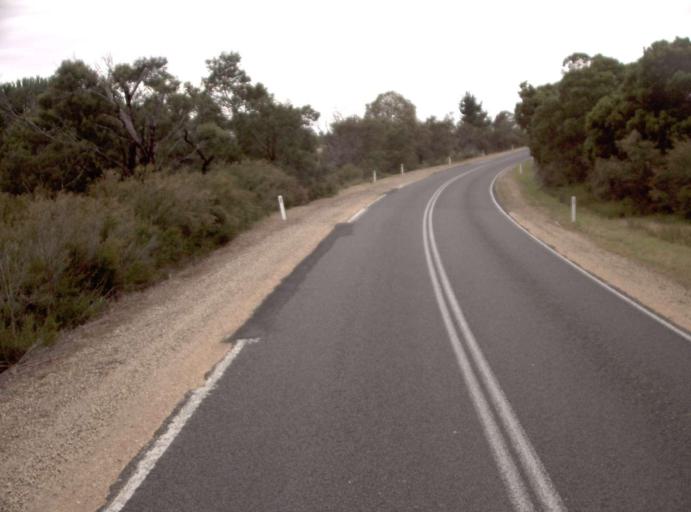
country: AU
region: Victoria
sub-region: Wellington
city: Sale
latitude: -38.1729
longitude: 147.1698
